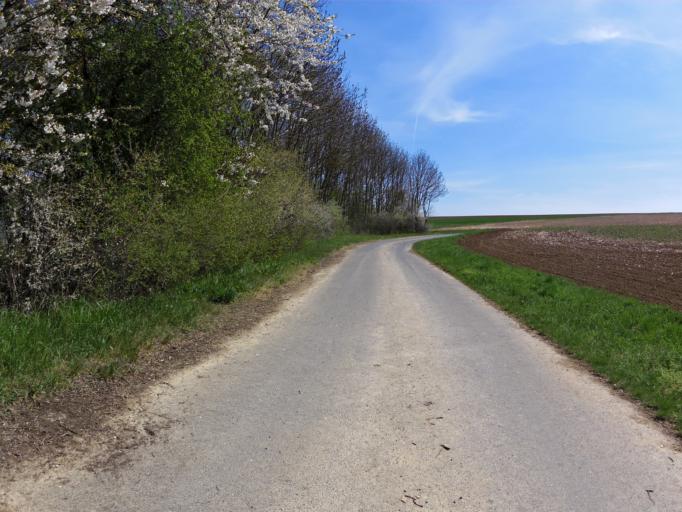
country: DE
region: Bavaria
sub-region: Regierungsbezirk Unterfranken
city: Mainstockheim
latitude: 49.7932
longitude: 10.1366
